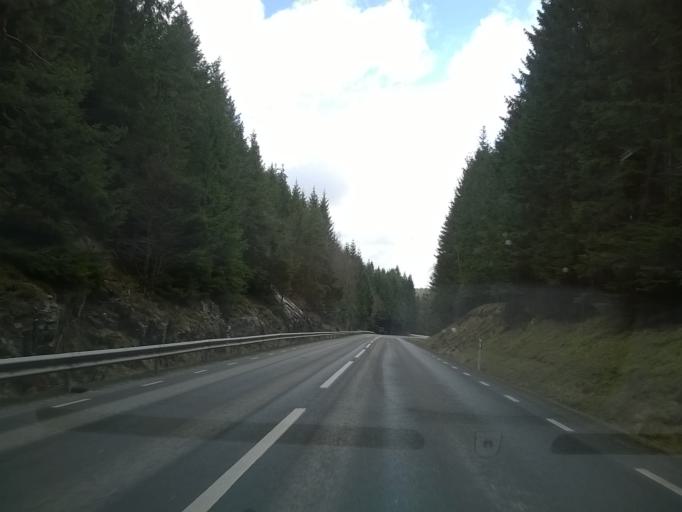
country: SE
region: Vaestra Goetaland
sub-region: Marks Kommun
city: Horred
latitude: 57.1568
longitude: 12.6632
